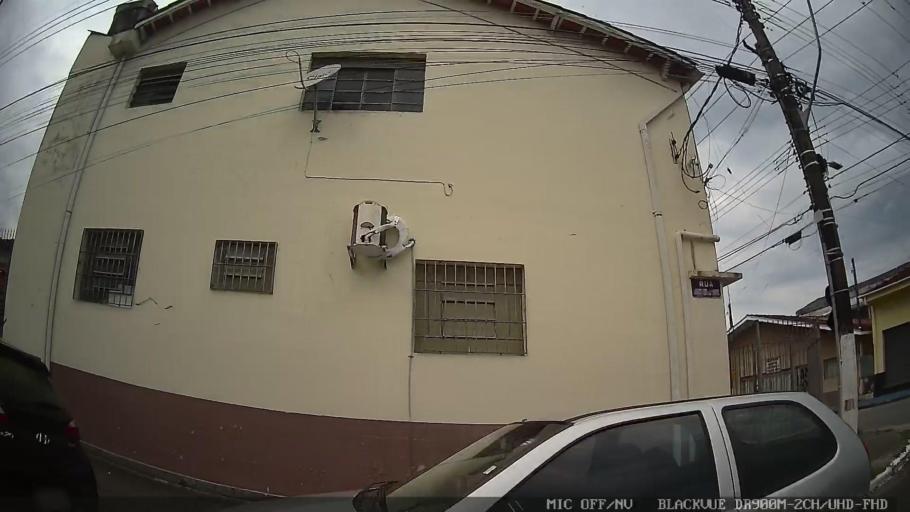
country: BR
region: Sao Paulo
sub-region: Caraguatatuba
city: Caraguatatuba
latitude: -23.6214
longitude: -45.4164
